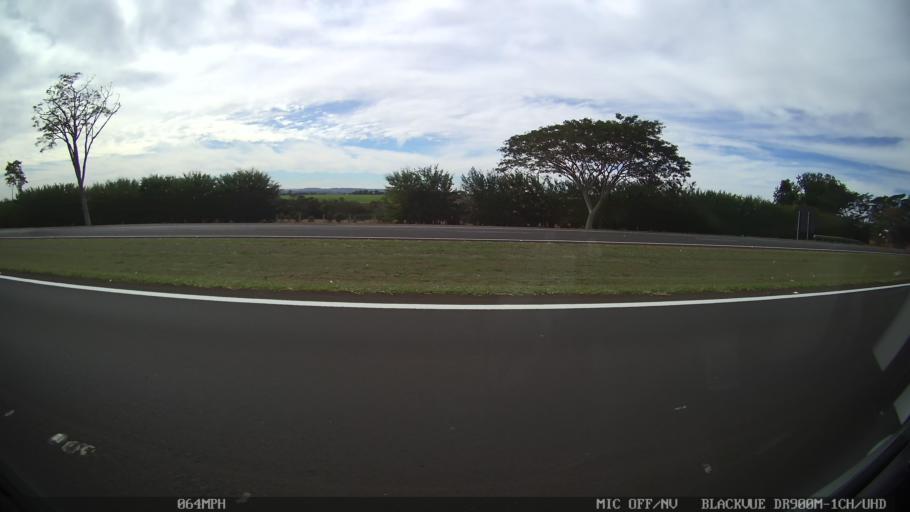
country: BR
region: Sao Paulo
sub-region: Taquaritinga
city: Taquaritinga
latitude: -21.4657
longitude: -48.6131
